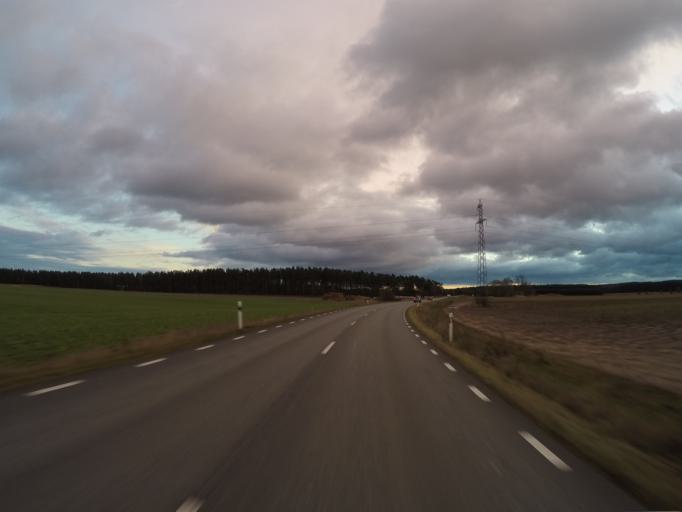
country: SE
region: Skane
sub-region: Kristianstads Kommun
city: Degeberga
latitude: 55.8873
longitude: 14.0871
